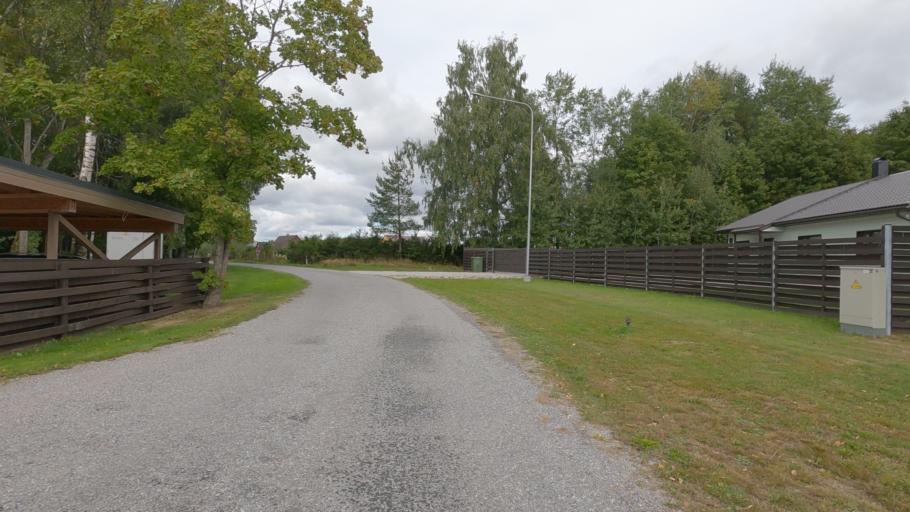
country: EE
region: Raplamaa
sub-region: Rapla vald
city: Rapla
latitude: 58.9917
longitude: 24.7927
